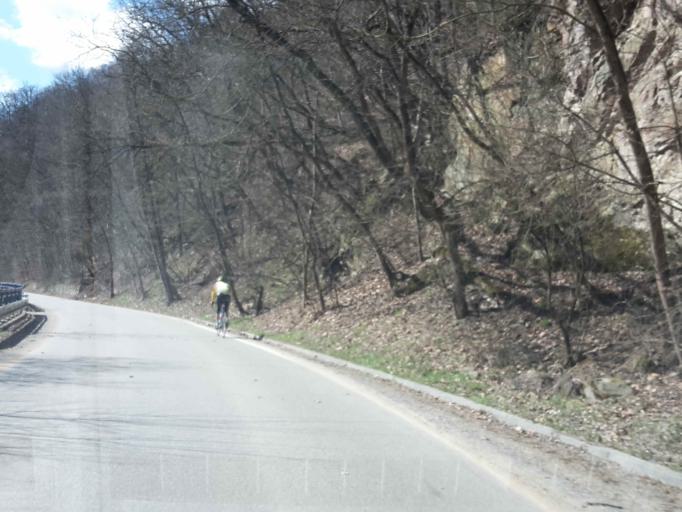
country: CZ
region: South Moravian
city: Bilovice nad Svitavou
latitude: 49.2781
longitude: 16.6734
